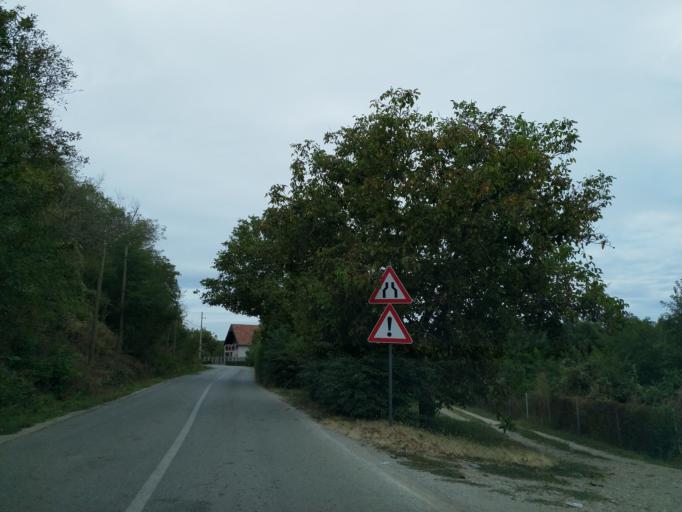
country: RS
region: Central Serbia
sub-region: Pomoravski Okrug
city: Cuprija
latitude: 43.9351
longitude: 21.3219
